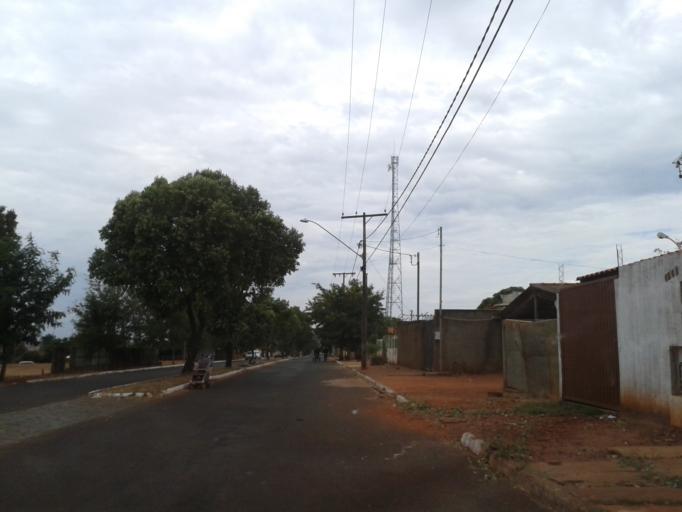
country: BR
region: Minas Gerais
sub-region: Santa Vitoria
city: Santa Vitoria
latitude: -18.8472
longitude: -50.1220
